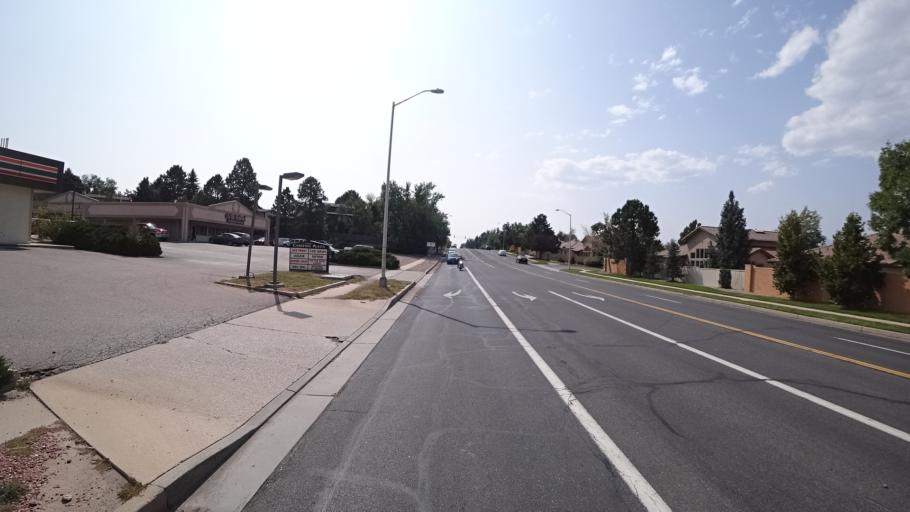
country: US
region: Colorado
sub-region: El Paso County
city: Cimarron Hills
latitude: 38.8736
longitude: -104.7478
